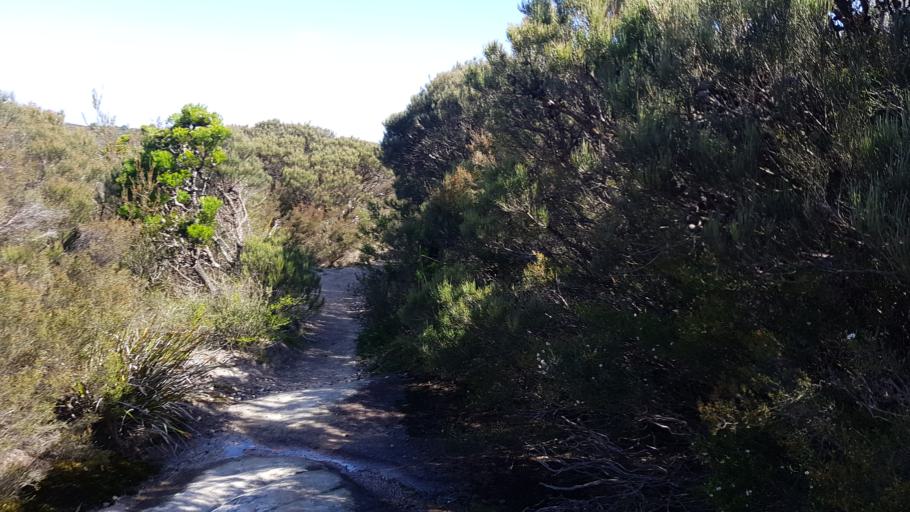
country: AU
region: New South Wales
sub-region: Blue Mountains Municipality
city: Katoomba
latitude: -33.9862
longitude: 150.1190
